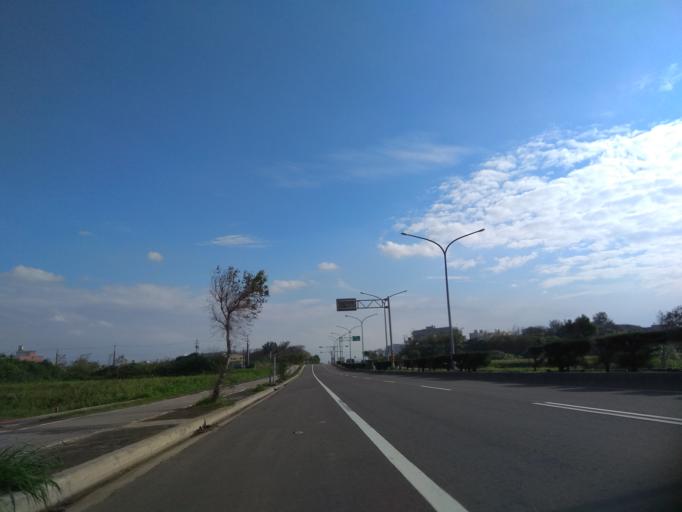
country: TW
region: Taiwan
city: Taoyuan City
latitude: 25.0793
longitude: 121.1691
